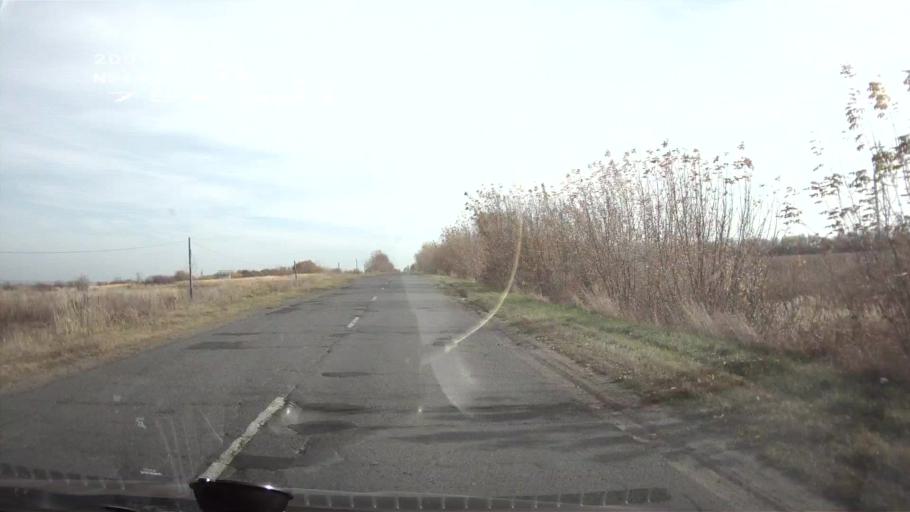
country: RU
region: Chuvashia
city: Alatyr'
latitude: 54.8451
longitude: 46.4613
